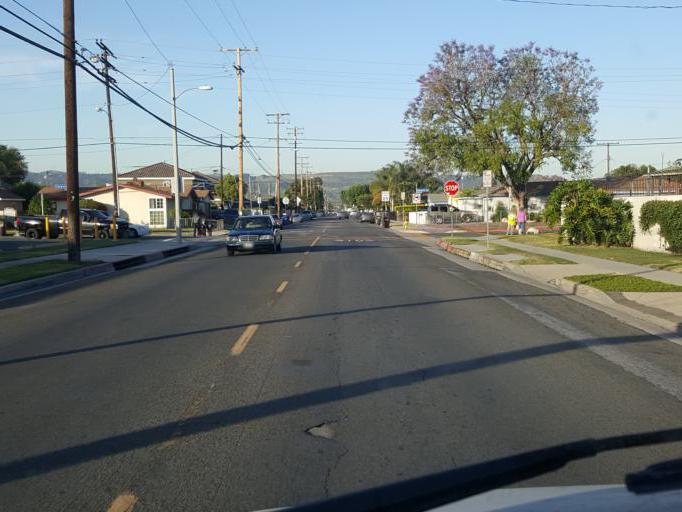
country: US
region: California
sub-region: Los Angeles County
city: West Puente Valley
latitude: 34.0566
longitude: -117.9681
